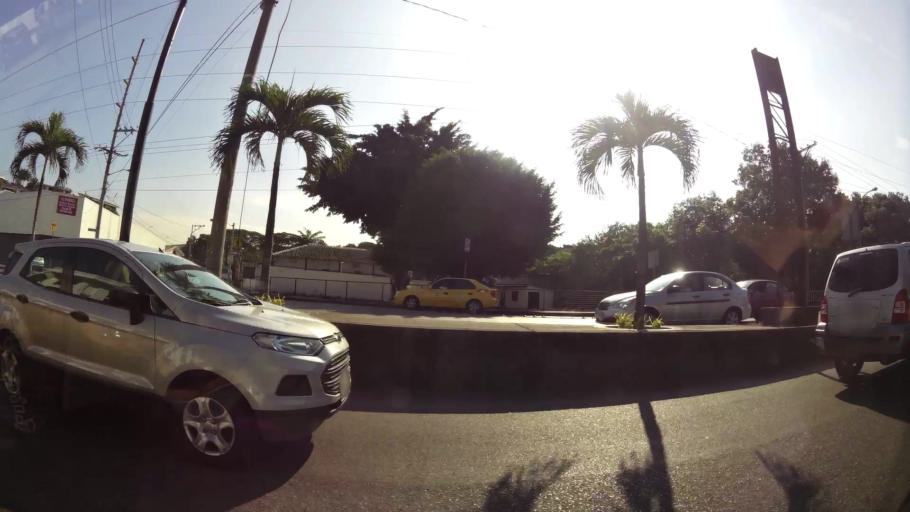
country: EC
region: Guayas
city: Guayaquil
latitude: -2.1681
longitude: -79.9020
